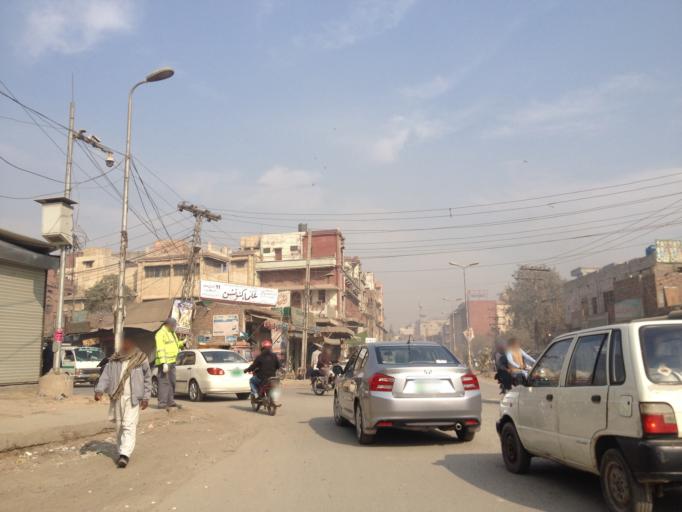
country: PK
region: Punjab
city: Lahore
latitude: 31.5625
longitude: 74.3084
